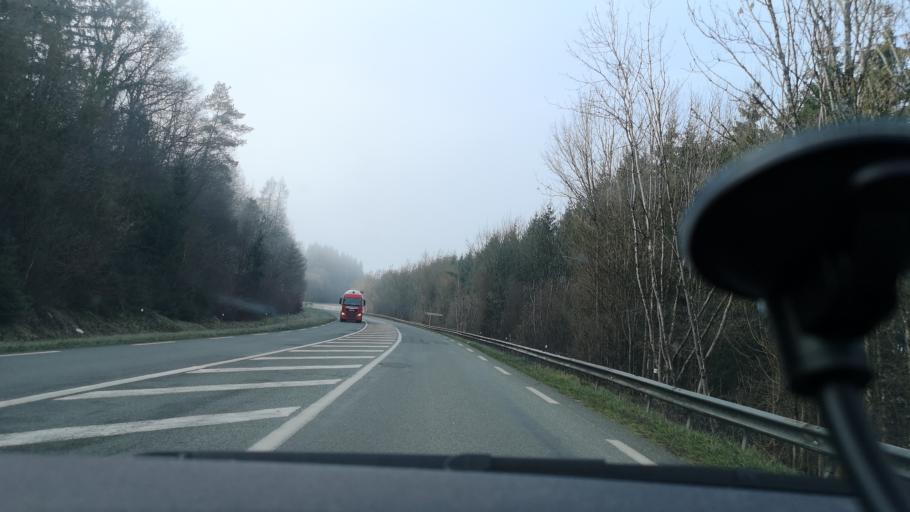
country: FR
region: Franche-Comte
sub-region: Departement du Doubs
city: Clerval
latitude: 47.4123
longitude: 6.5427
